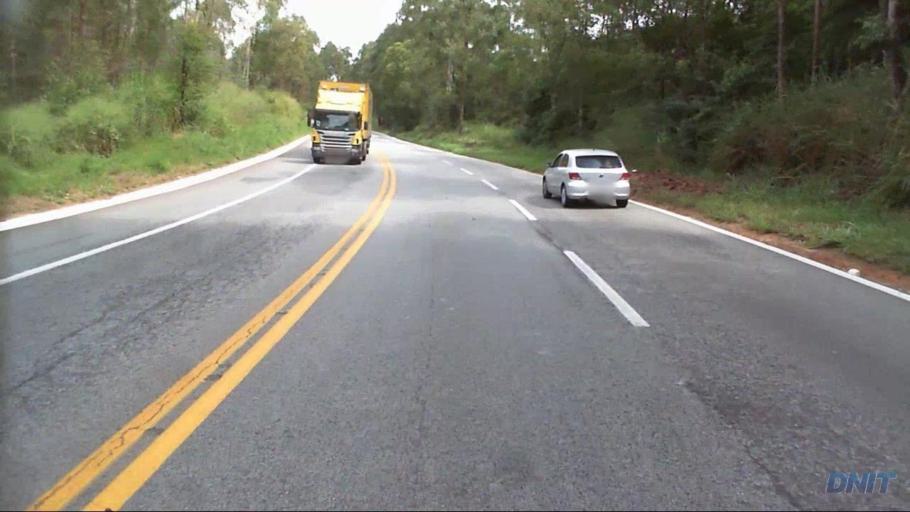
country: BR
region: Minas Gerais
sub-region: Caete
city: Caete
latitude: -19.7271
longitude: -43.5930
